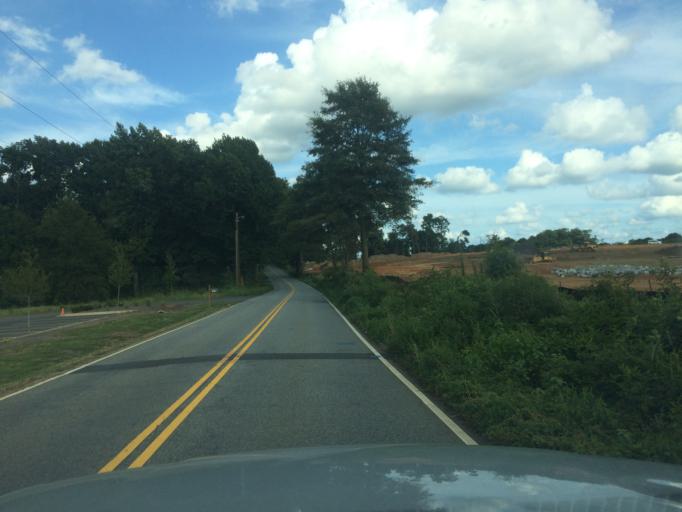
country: US
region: South Carolina
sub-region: Spartanburg County
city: Duncan
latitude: 34.8609
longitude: -82.1370
